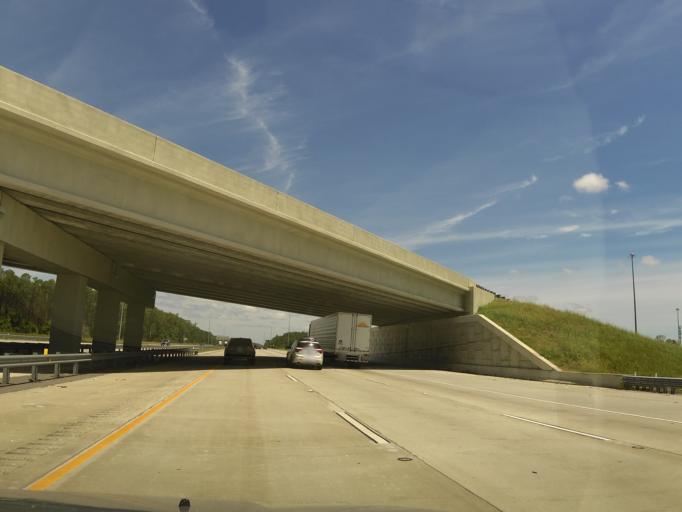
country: US
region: Georgia
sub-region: McIntosh County
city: Darien
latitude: 31.3057
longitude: -81.4800
